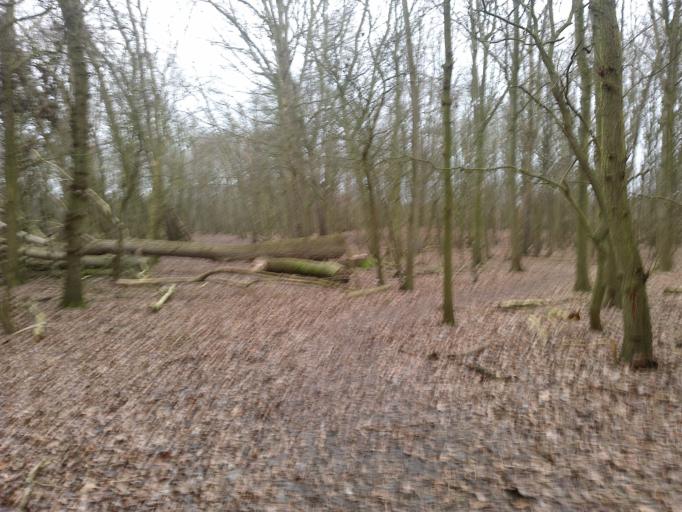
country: NL
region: South Holland
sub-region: Gemeente Noordwijkerhout
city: Noordwijkerhout
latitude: 52.2958
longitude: 4.4984
